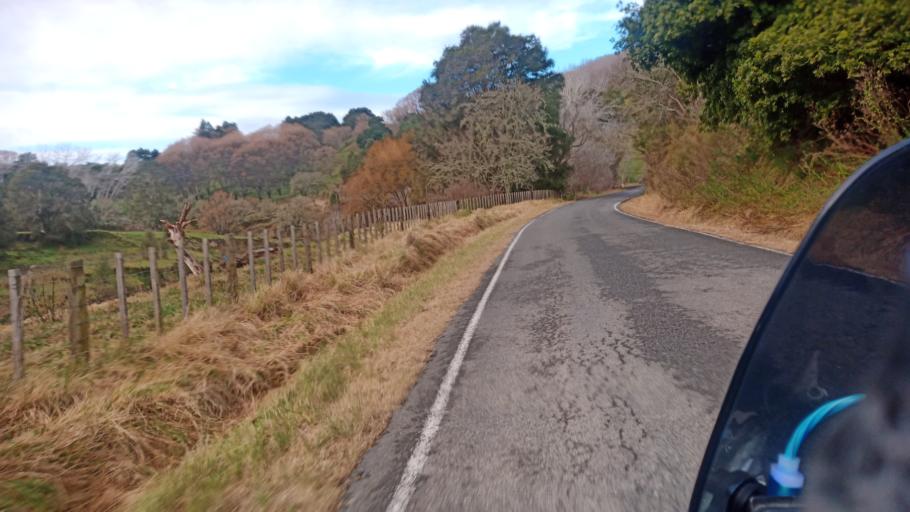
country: NZ
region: Gisborne
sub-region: Gisborne District
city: Gisborne
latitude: -38.4101
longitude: 177.9339
